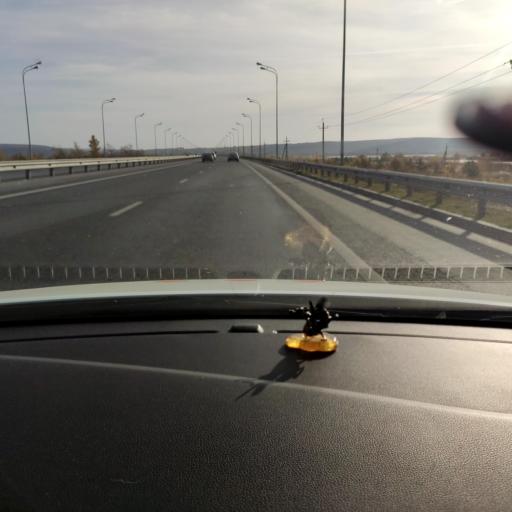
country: RU
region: Tatarstan
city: Osinovo
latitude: 55.8143
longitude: 48.8420
